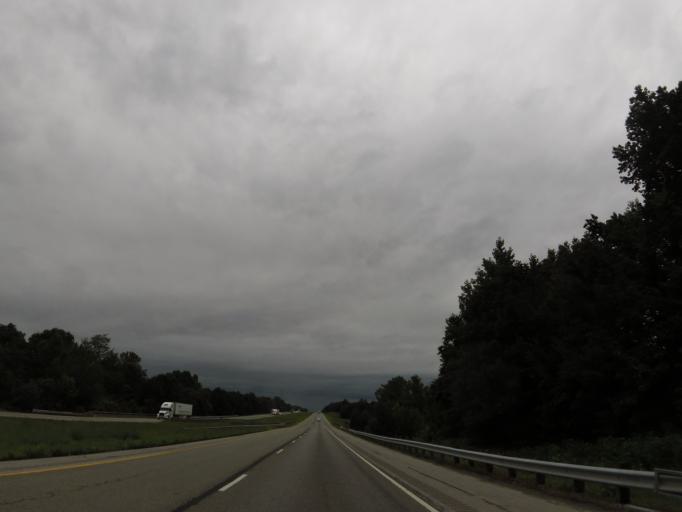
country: US
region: Illinois
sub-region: Massac County
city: Metropolis
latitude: 37.2263
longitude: -88.7060
